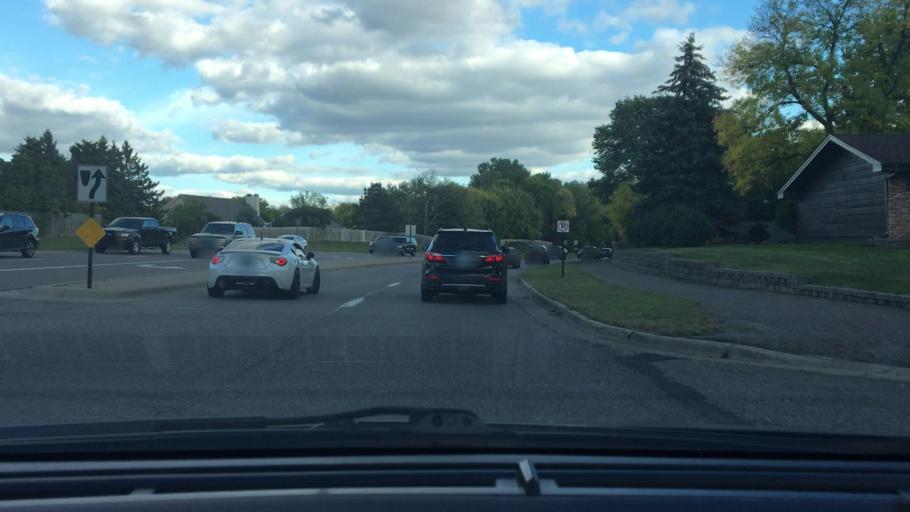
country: US
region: Minnesota
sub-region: Hennepin County
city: Maple Grove
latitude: 45.0617
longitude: -93.4344
